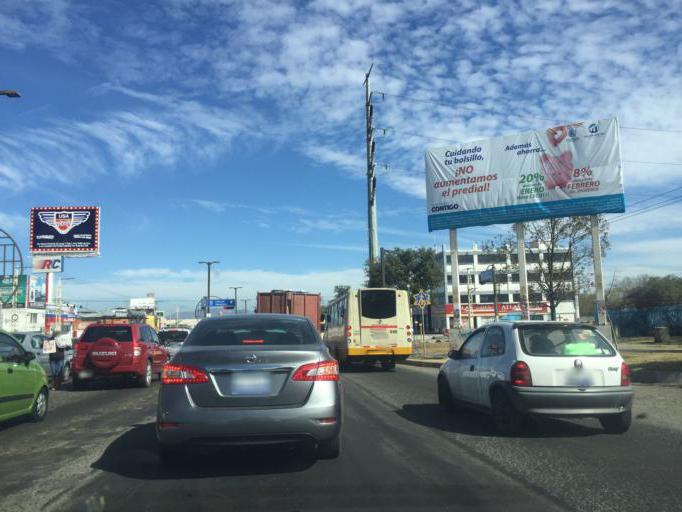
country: MX
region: Queretaro
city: San Juan del Rio
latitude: 20.3825
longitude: -99.9852
